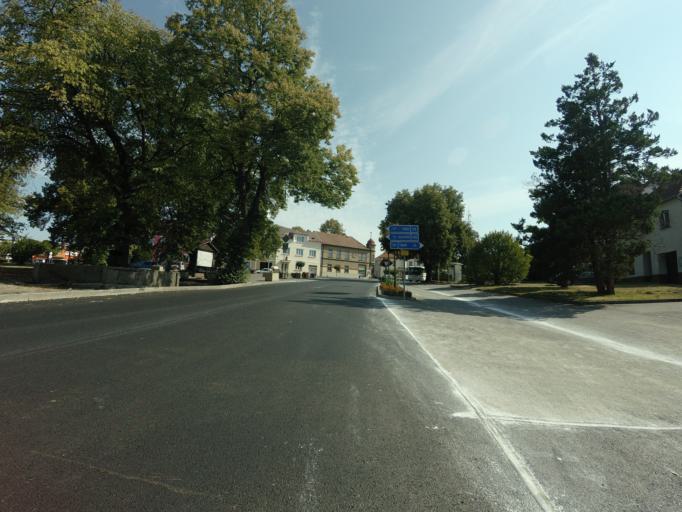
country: CZ
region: Jihocesky
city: Bernartice
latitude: 49.3685
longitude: 14.3800
